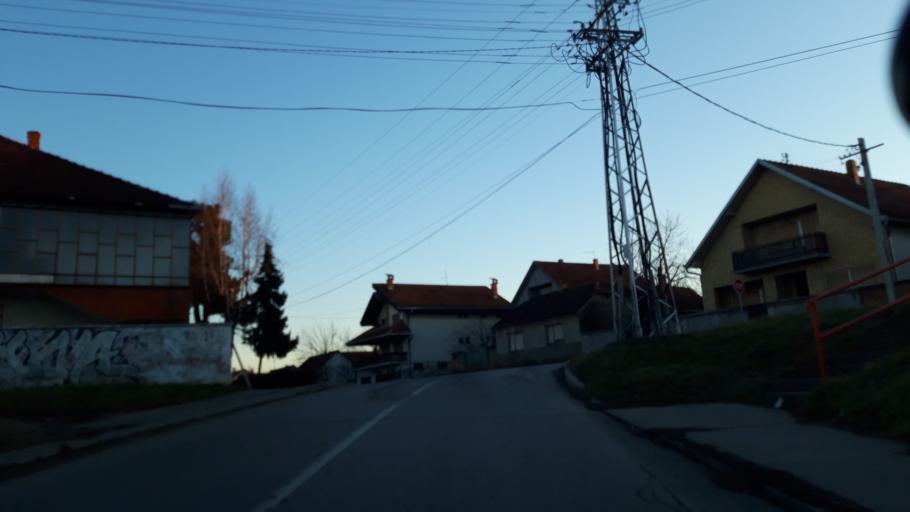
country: RS
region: Autonomna Pokrajina Vojvodina
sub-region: Sremski Okrug
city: Ingija
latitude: 45.0501
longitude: 20.0681
